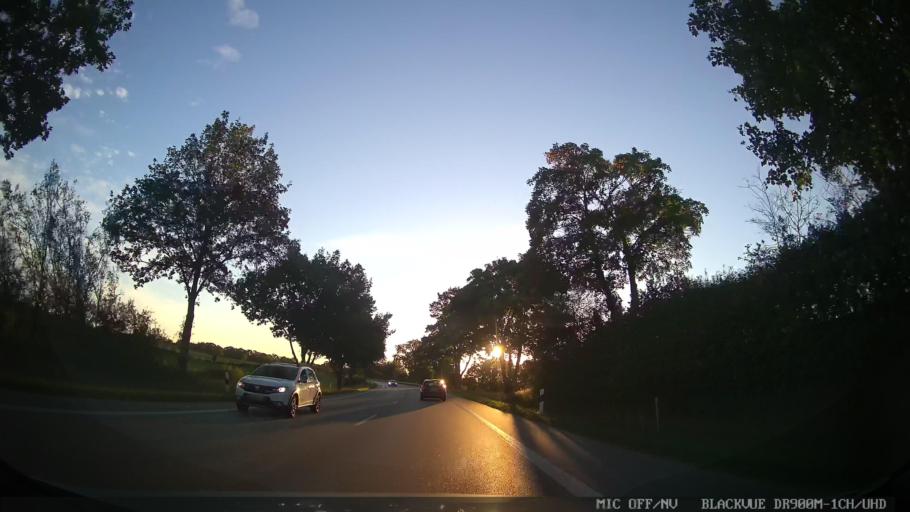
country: DE
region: Schleswig-Holstein
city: Gromitz
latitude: 54.1484
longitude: 10.9389
